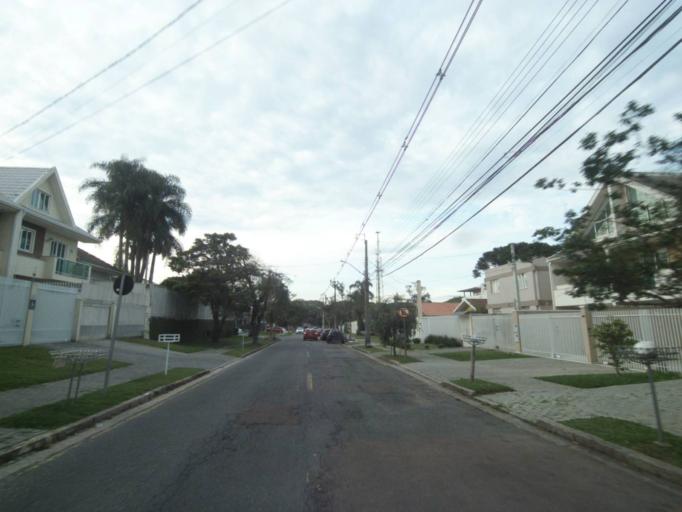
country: BR
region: Parana
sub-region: Curitiba
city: Curitiba
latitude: -25.4293
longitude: -49.2371
